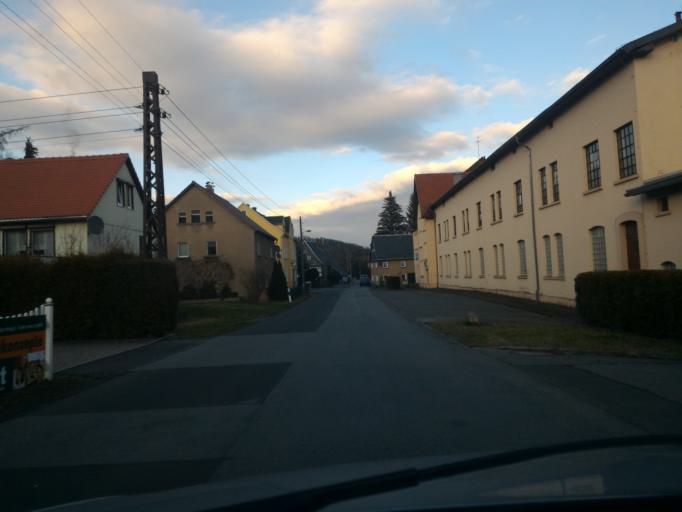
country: DE
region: Saxony
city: Hainewalde
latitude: 50.9160
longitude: 14.7121
